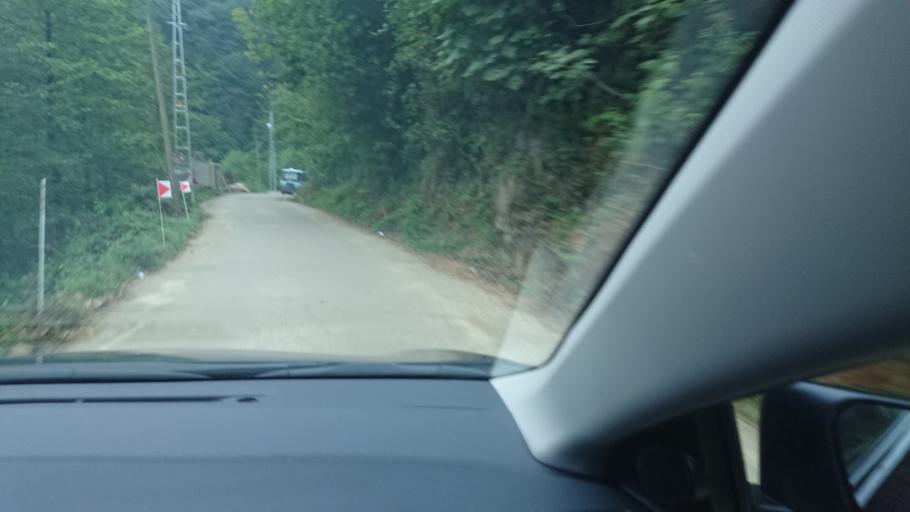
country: TR
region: Rize
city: Cayeli
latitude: 41.0475
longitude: 40.8004
